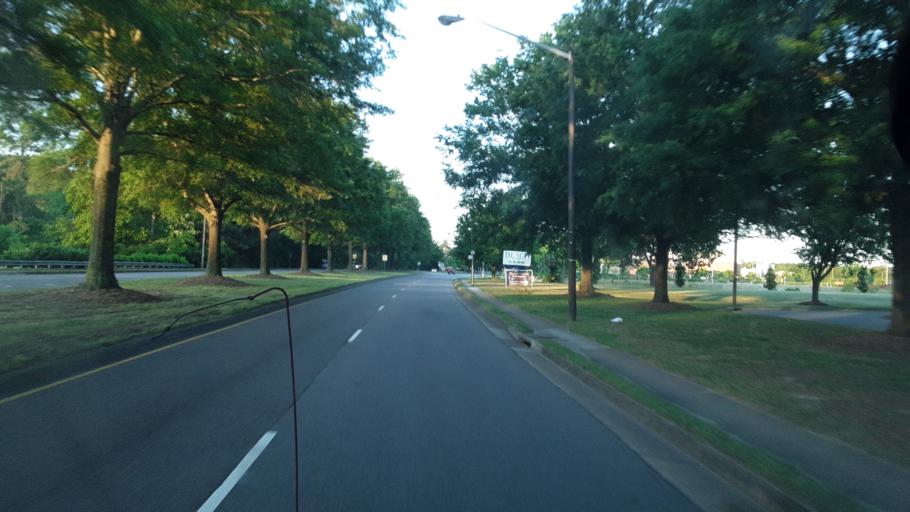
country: US
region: Virginia
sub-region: City of Virginia Beach
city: Virginia Beach
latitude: 36.7788
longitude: -76.0032
